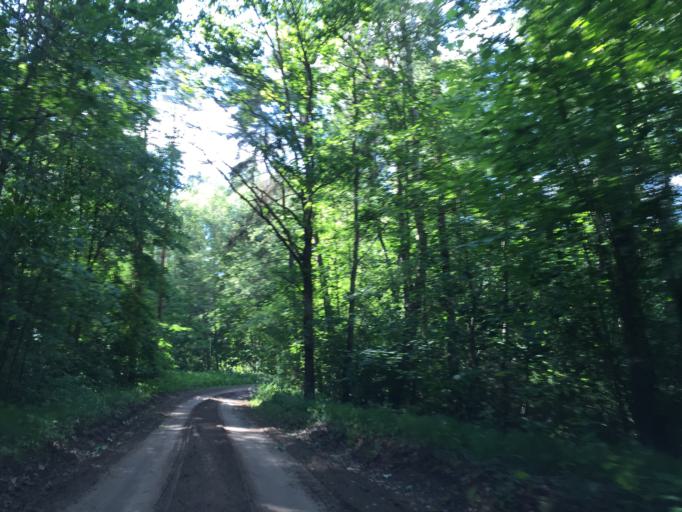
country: LV
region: Vecumnieki
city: Vecumnieki
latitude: 56.4368
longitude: 24.5932
